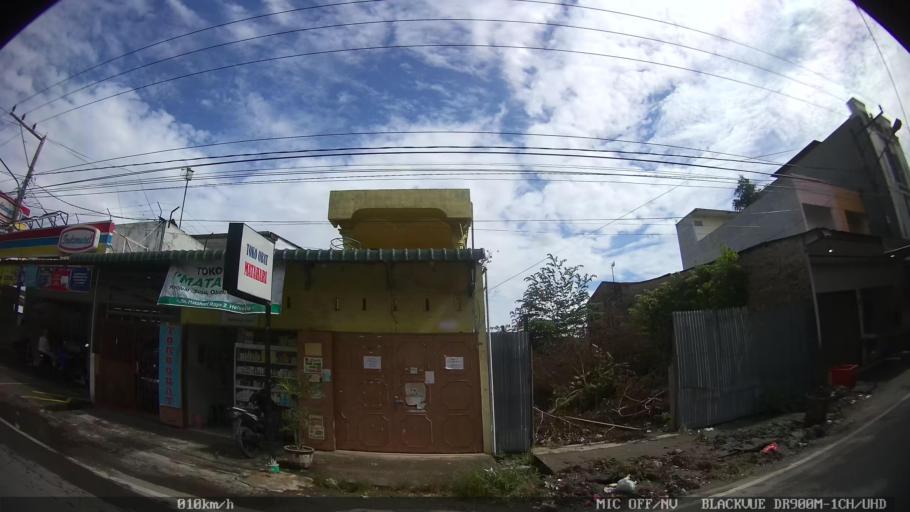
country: ID
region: North Sumatra
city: Sunggal
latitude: 3.6109
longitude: 98.6314
